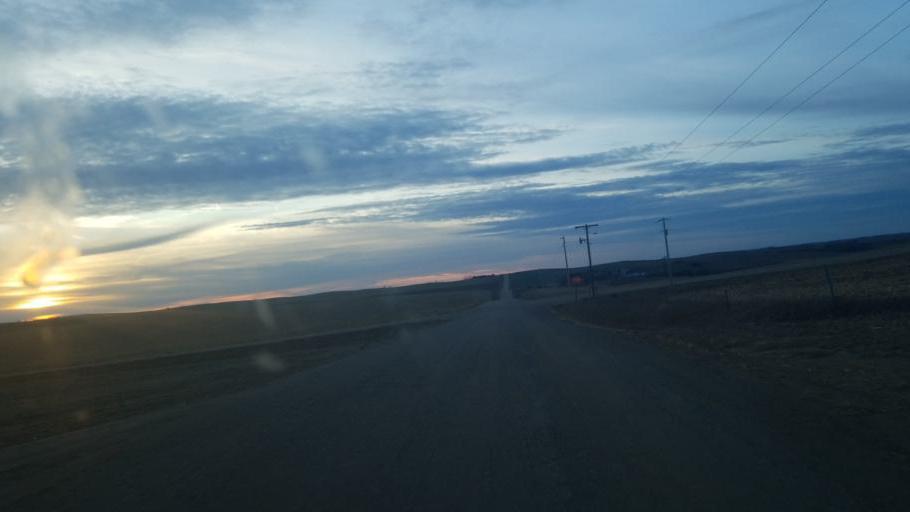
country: US
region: Nebraska
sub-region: Knox County
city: Bloomfield
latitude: 42.6846
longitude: -97.7392
